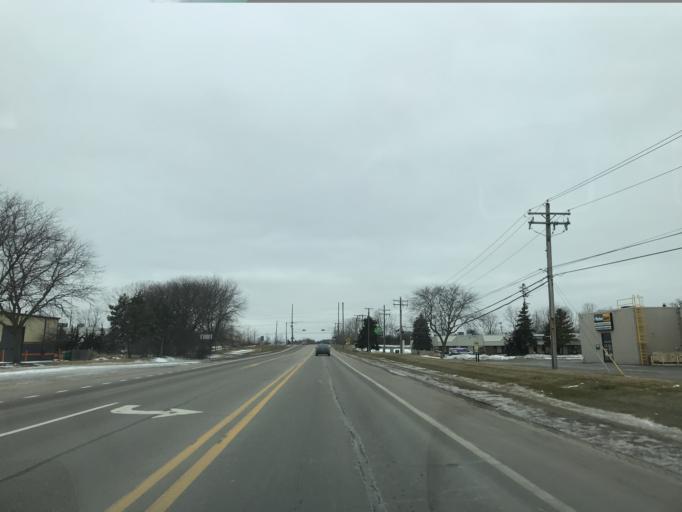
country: US
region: Michigan
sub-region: Washtenaw County
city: Ann Arbor
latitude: 42.2297
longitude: -83.7261
